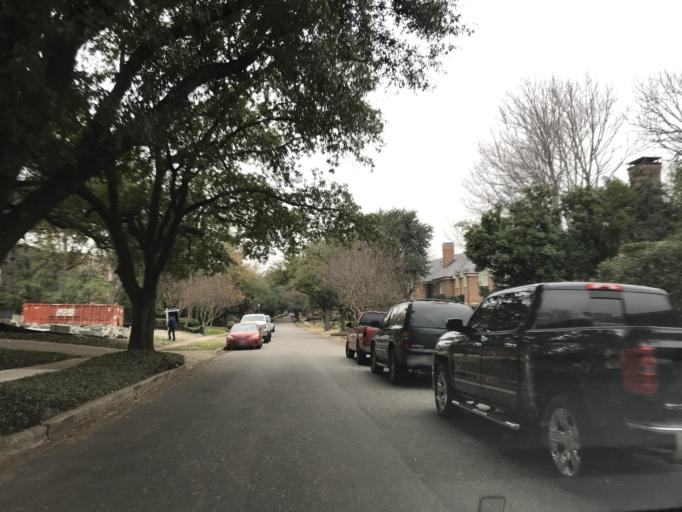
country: US
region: Texas
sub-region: Dallas County
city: Highland Park
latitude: 32.8248
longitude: -96.8106
